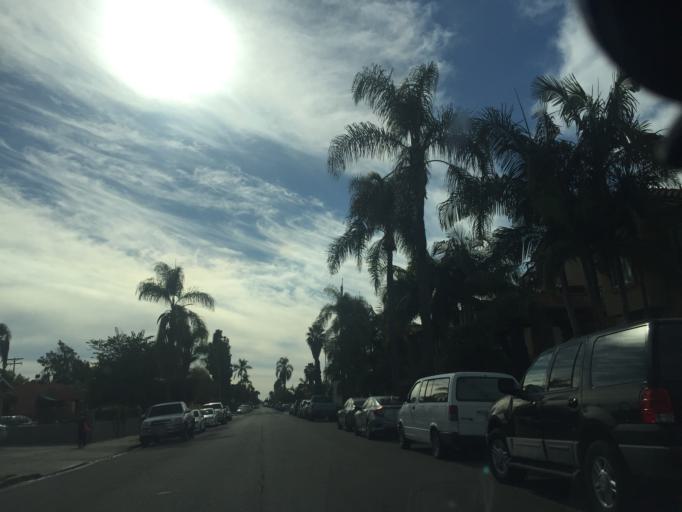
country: US
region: California
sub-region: San Diego County
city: Lemon Grove
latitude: 32.7541
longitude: -117.0944
